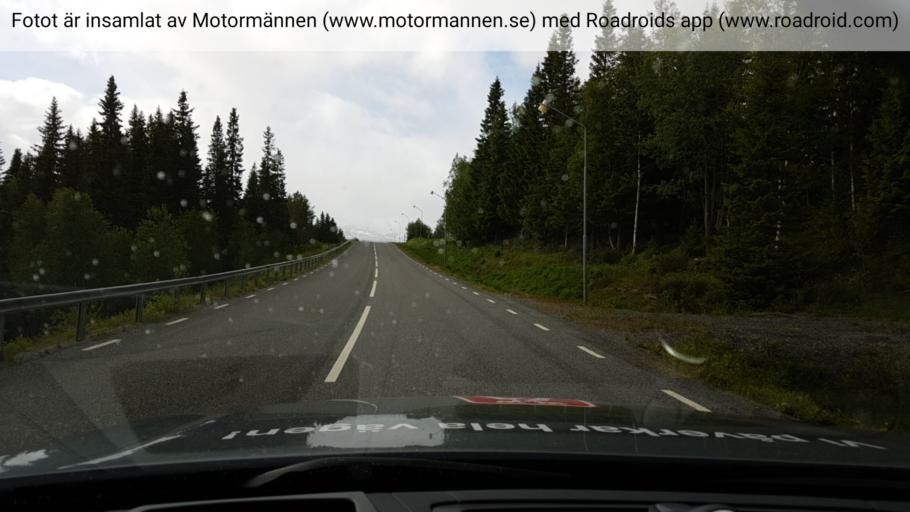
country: SE
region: Jaemtland
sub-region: Are Kommun
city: Are
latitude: 63.6610
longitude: 13.0564
